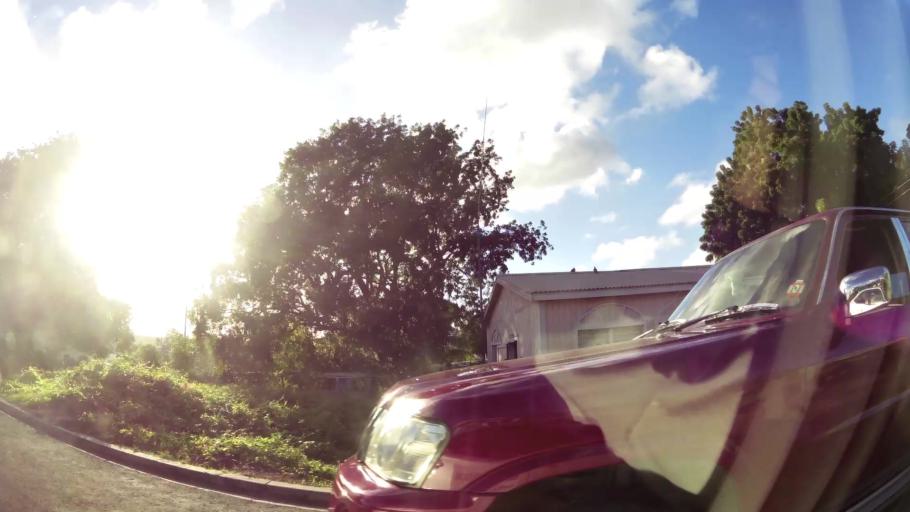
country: AG
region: Saint George
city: Piggotts
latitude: 17.1239
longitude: -61.8021
